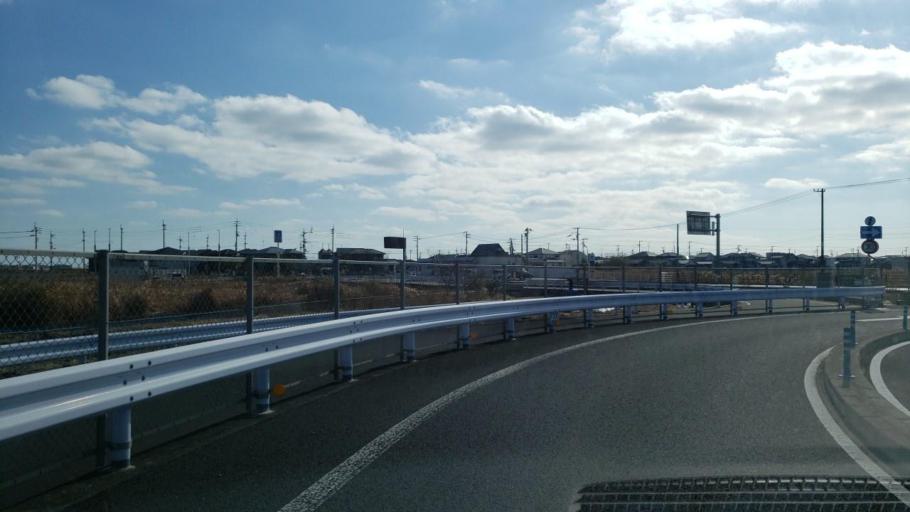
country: JP
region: Tokushima
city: Narutocho-mitsuishi
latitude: 34.1416
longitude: 134.5658
